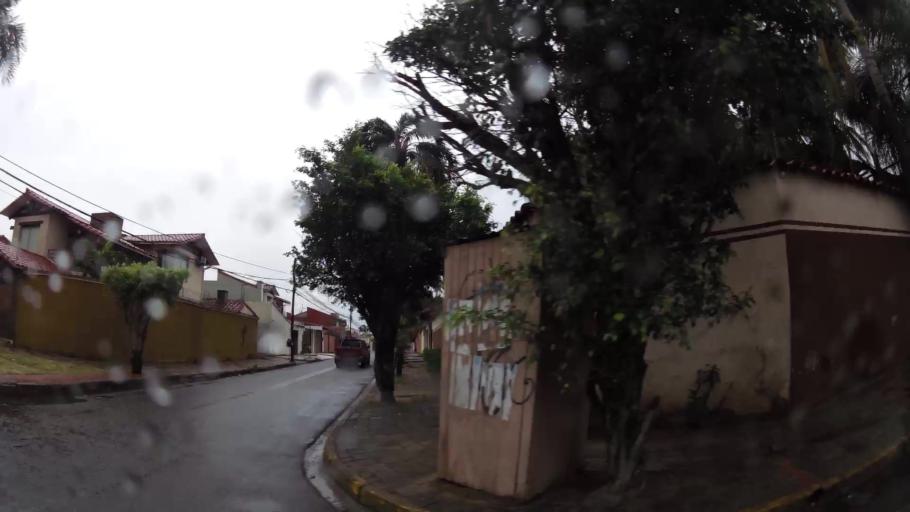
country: BO
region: Santa Cruz
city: Santa Cruz de la Sierra
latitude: -17.7700
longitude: -63.1515
